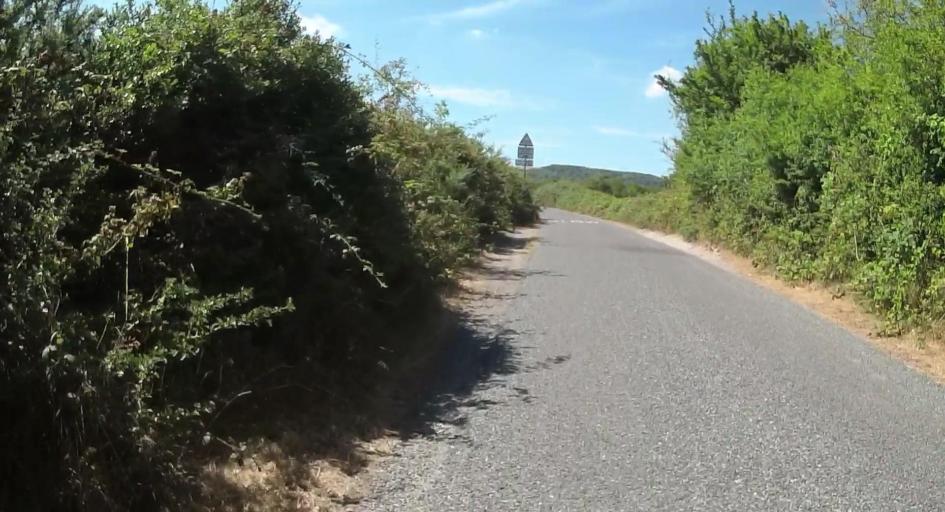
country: GB
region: England
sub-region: Dorset
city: Wareham
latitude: 50.6546
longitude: -2.0612
